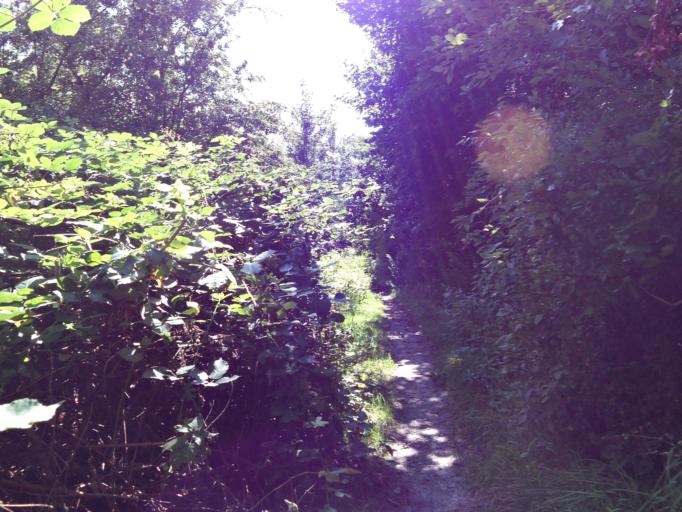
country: DE
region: Saxony
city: Rackwitz
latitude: 51.3872
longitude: 12.4013
